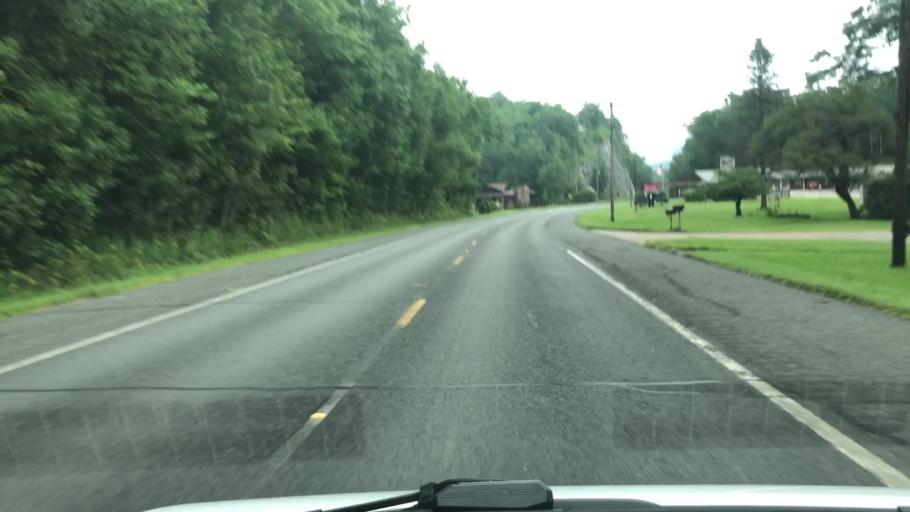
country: US
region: Massachusetts
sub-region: Berkshire County
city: Lanesborough
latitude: 42.5916
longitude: -73.2476
